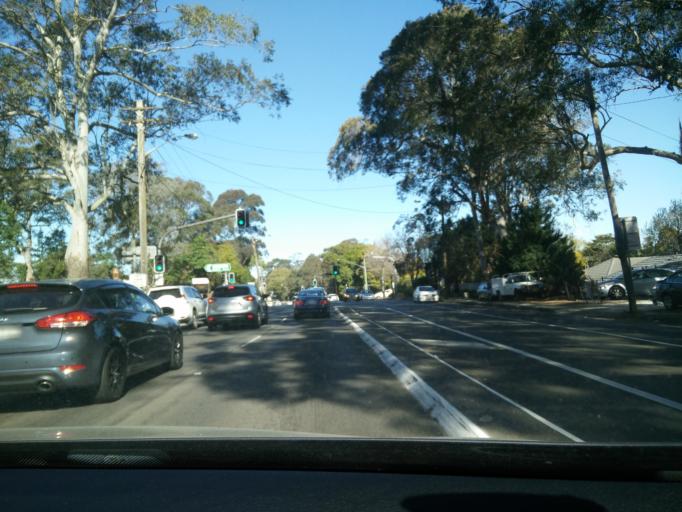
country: AU
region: New South Wales
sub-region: City of Sydney
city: Pymble
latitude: -33.7392
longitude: 151.1360
